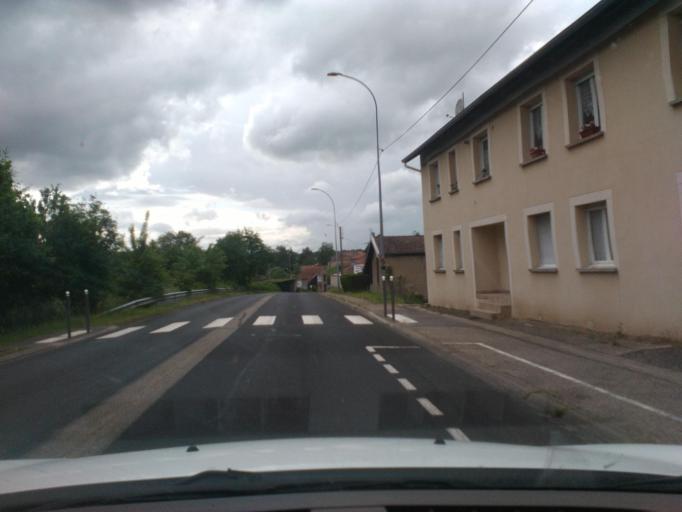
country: FR
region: Lorraine
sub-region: Departement de Meurthe-et-Moselle
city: Baccarat
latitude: 48.4410
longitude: 6.7545
